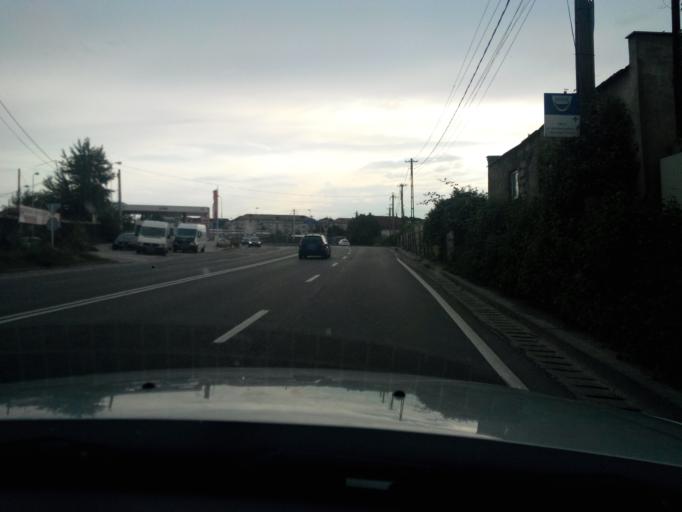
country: RO
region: Arges
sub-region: Comuna Bascov
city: Bascov
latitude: 44.8930
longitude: 24.8272
